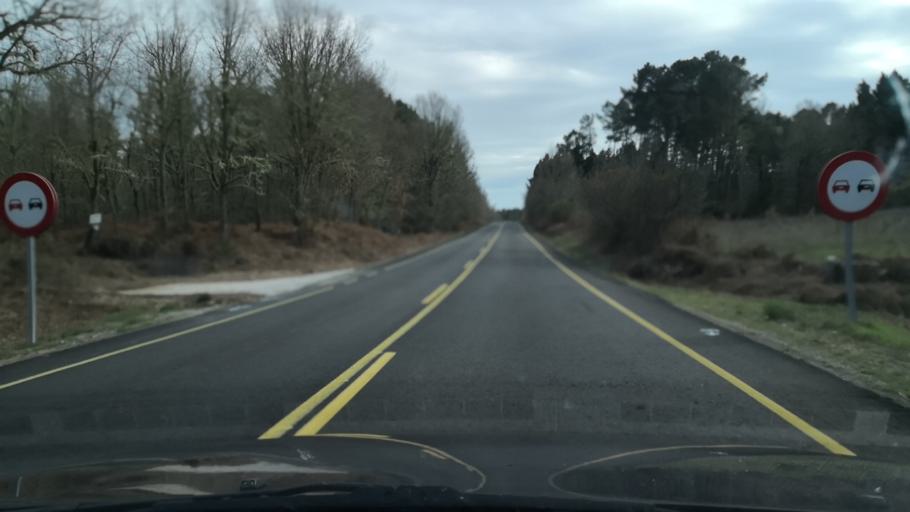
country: ES
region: Castille and Leon
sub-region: Provincia de Salamanca
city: Penaparda
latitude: 40.3080
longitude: -6.6502
